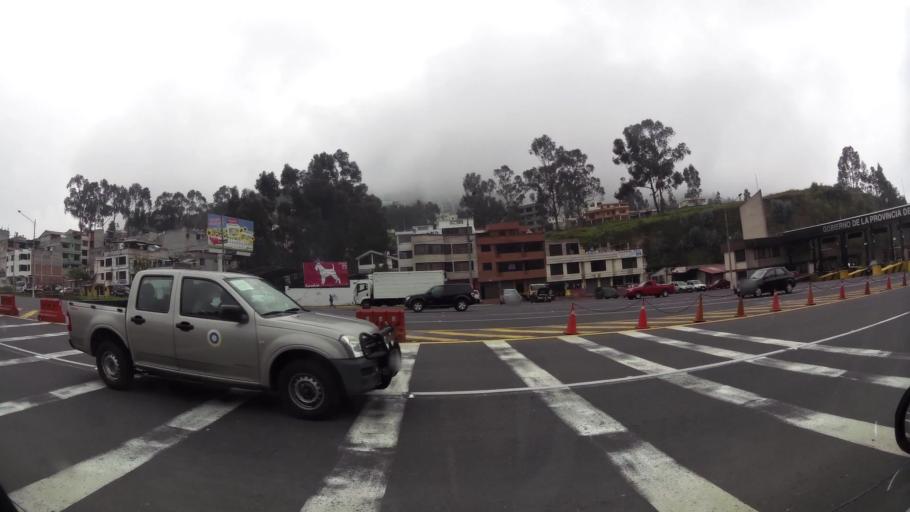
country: EC
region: Pichincha
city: Quito
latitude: -0.2432
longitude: -78.4856
